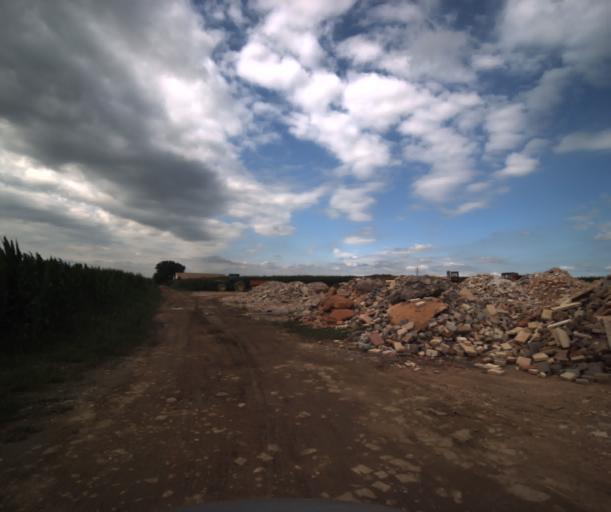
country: FR
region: Midi-Pyrenees
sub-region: Departement de la Haute-Garonne
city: Longages
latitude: 43.3800
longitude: 1.2288
